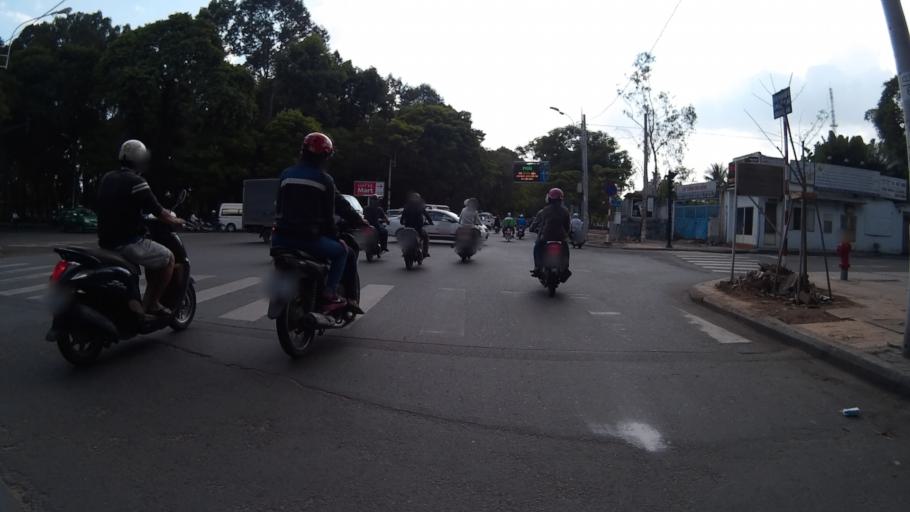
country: VN
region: Ho Chi Minh City
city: Quan Phu Nhuan
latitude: 10.8030
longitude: 106.6635
